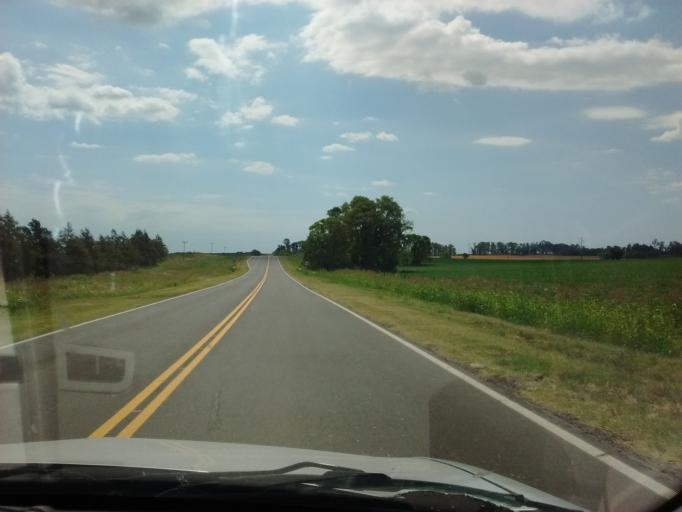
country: AR
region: Entre Rios
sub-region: Departamento de Victoria
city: Victoria
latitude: -32.6588
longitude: -60.0568
